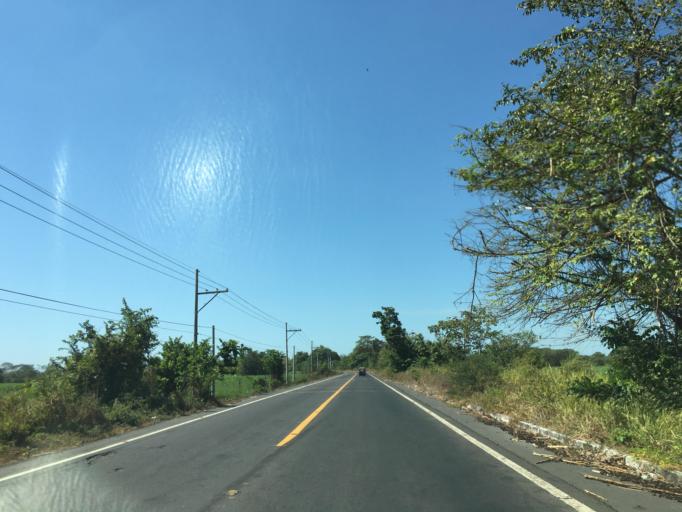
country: GT
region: Escuintla
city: Puerto San Jose
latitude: 14.0222
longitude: -90.8889
